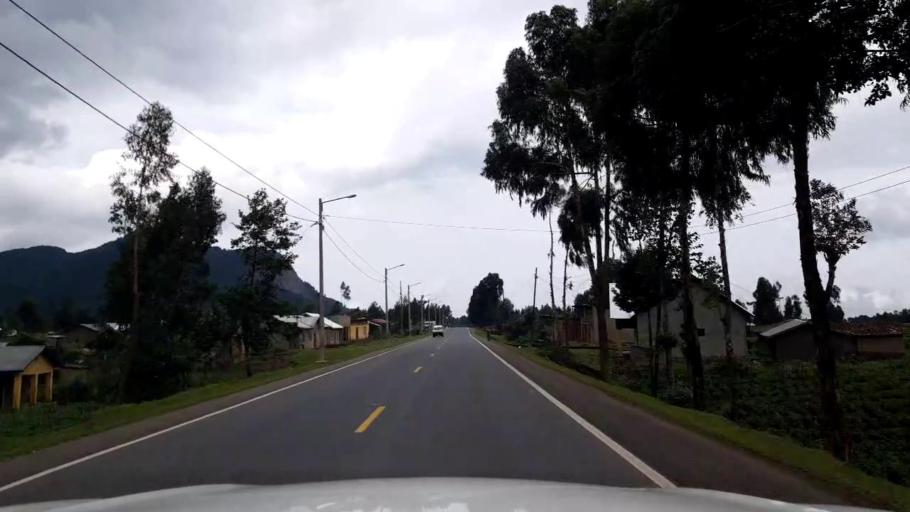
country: RW
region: Western Province
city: Gisenyi
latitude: -1.6353
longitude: 29.4084
